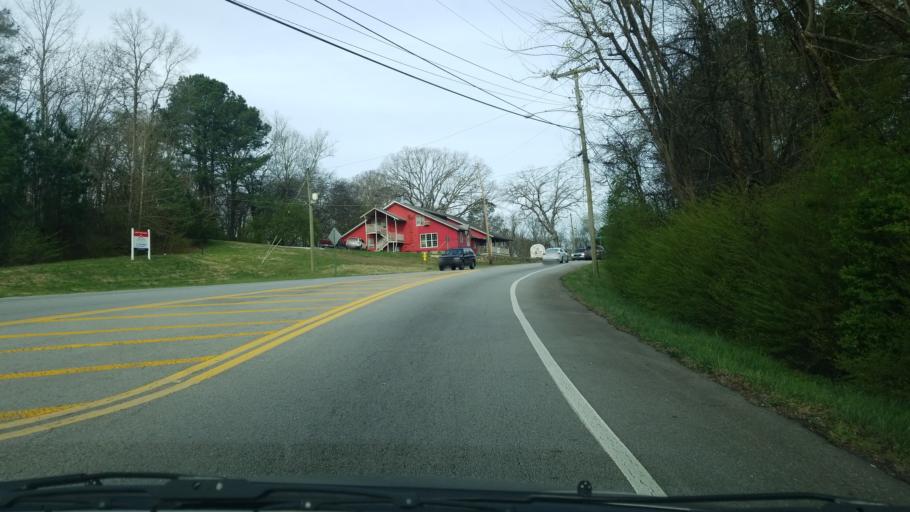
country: US
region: Tennessee
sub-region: Hamilton County
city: East Brainerd
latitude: 35.0169
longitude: -85.1835
